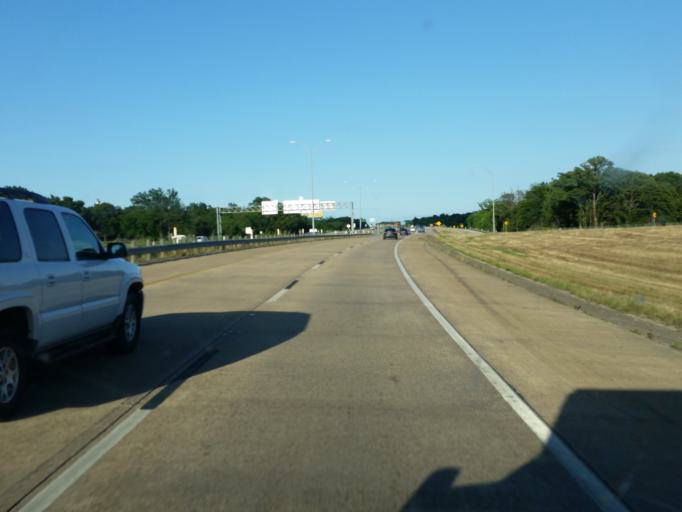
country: US
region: Texas
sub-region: Dallas County
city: Balch Springs
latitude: 32.7018
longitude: -96.6220
